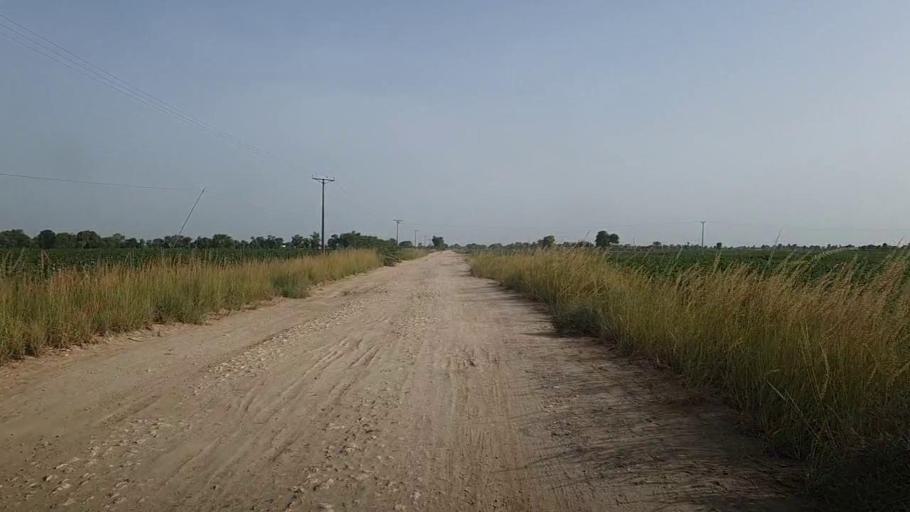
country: PK
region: Sindh
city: Pad Idan
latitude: 26.7666
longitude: 68.2572
